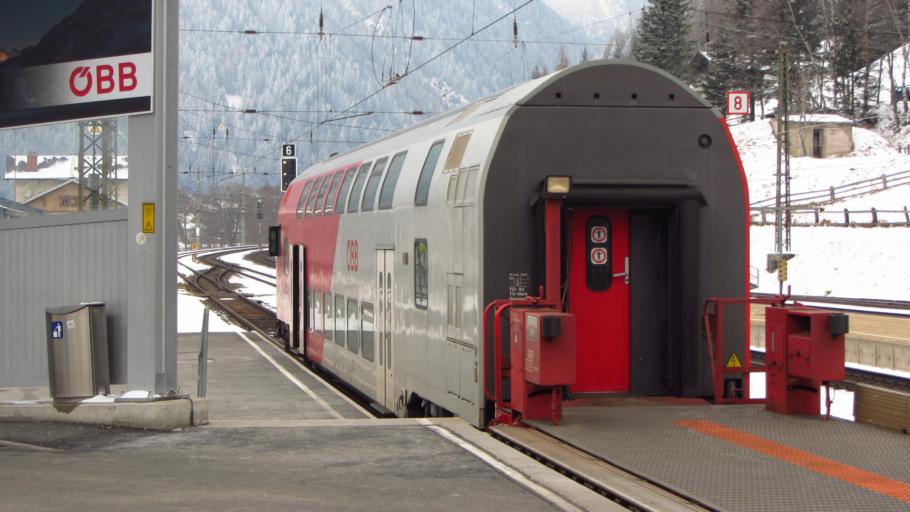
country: AT
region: Carinthia
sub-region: Politischer Bezirk Spittal an der Drau
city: Obervellach
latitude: 46.9807
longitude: 13.1766
